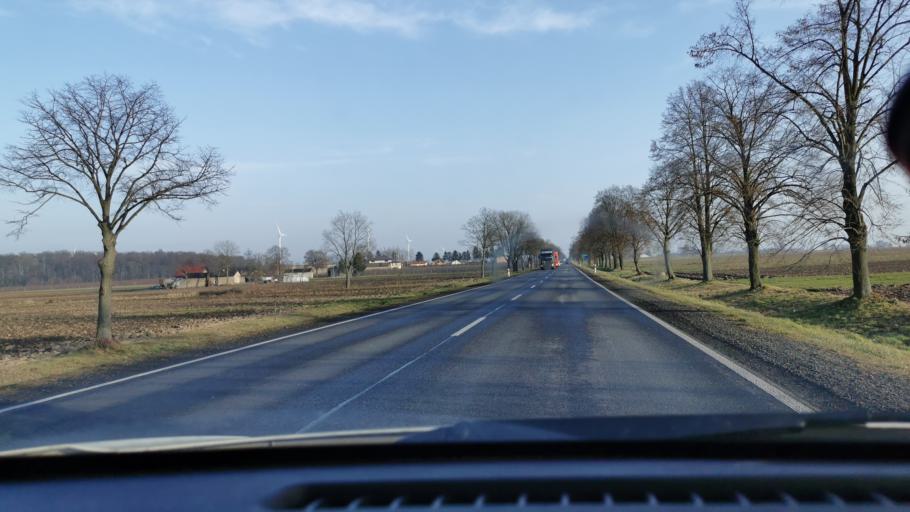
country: PL
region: Lodz Voivodeship
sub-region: Powiat sieradzki
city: Blaszki
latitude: 51.6395
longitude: 18.5070
